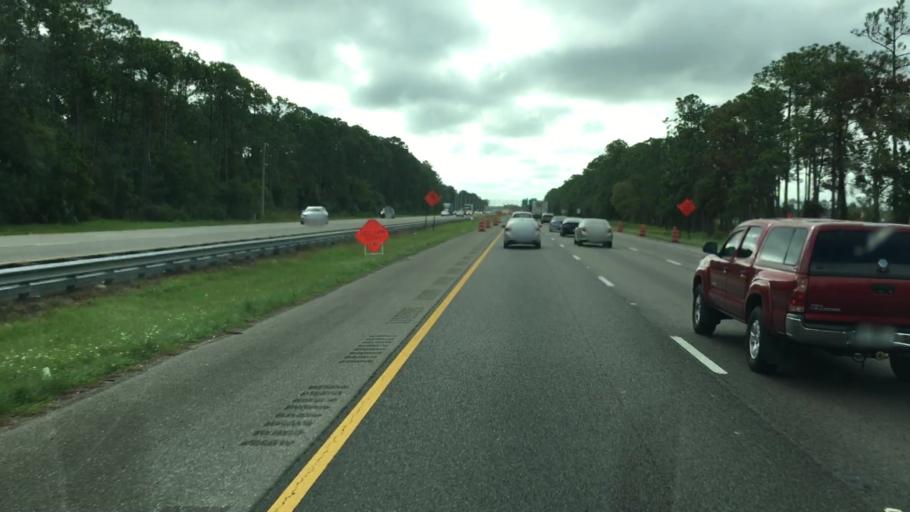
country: US
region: Florida
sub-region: Volusia County
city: Daytona Beach
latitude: 29.1924
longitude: -81.0936
